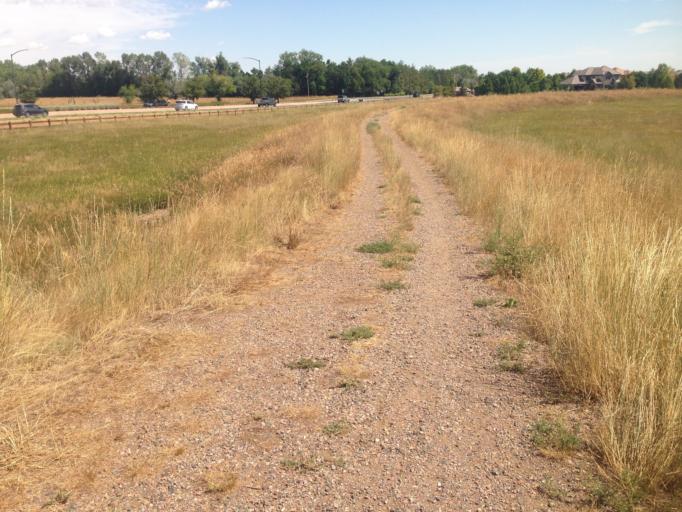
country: US
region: Colorado
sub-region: Adams County
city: Northglenn
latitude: 39.9569
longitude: -105.0091
